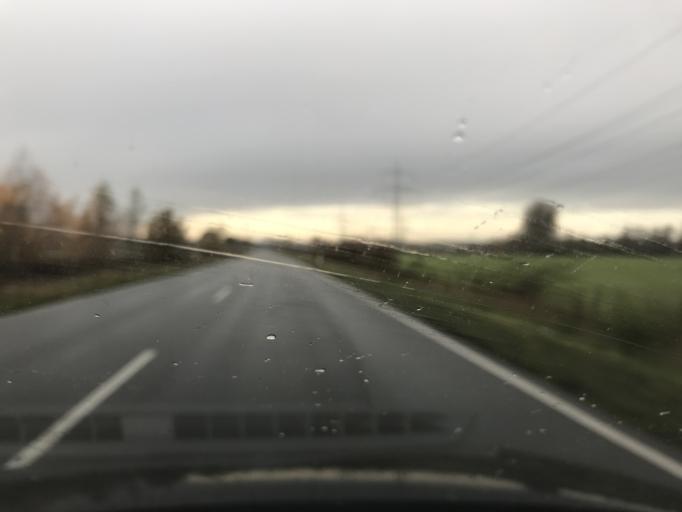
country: DE
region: North Rhine-Westphalia
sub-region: Regierungsbezirk Arnsberg
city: Hamm
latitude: 51.7239
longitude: 7.7745
